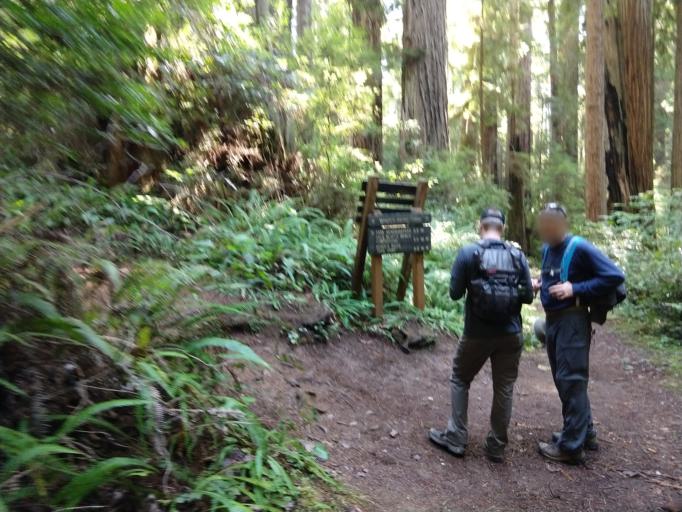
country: US
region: California
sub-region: Humboldt County
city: Westhaven-Moonstone
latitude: 41.3794
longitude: -124.0489
